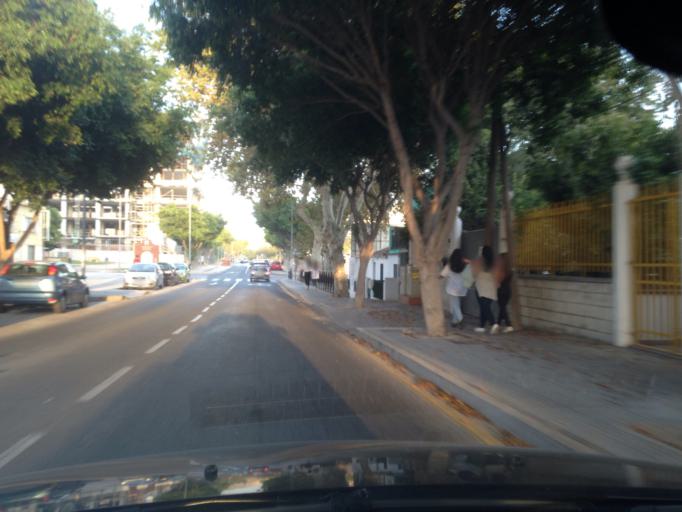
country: ES
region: Andalusia
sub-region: Provincia de Malaga
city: Malaga
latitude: 36.7253
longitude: -4.4650
